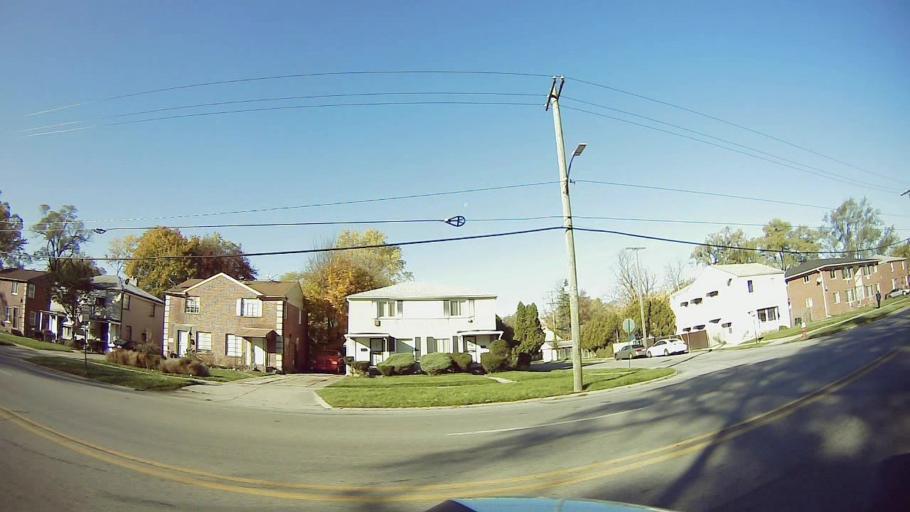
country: US
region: Michigan
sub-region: Oakland County
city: Oak Park
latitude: 42.4068
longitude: -83.1989
